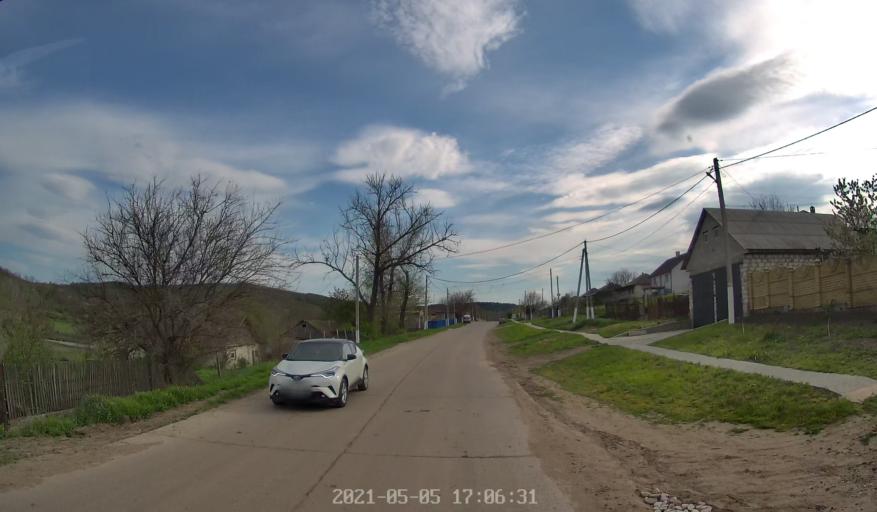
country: MD
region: Chisinau
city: Vadul lui Voda
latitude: 47.0195
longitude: 29.1392
